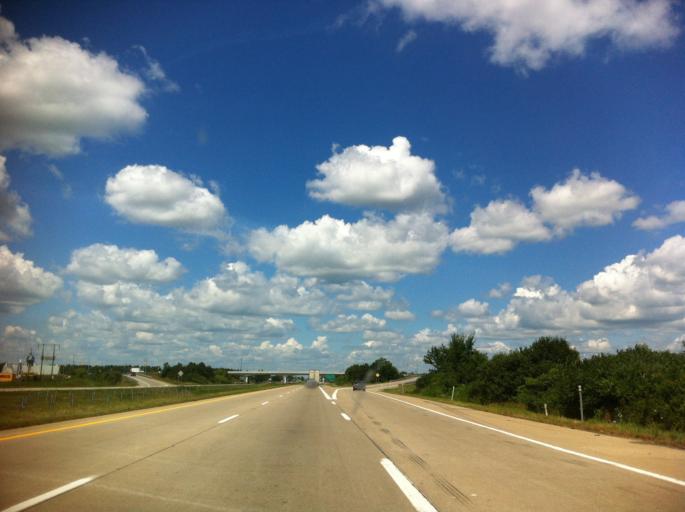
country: US
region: Ohio
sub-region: Lucas County
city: Sylvania
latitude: 41.7438
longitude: -83.6938
